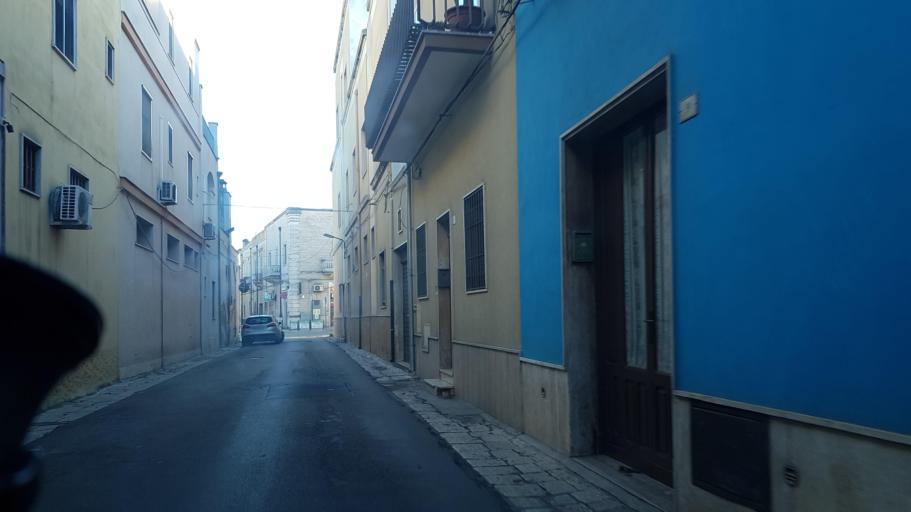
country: IT
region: Apulia
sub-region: Provincia di Brindisi
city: Latiano
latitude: 40.5521
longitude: 17.7171
